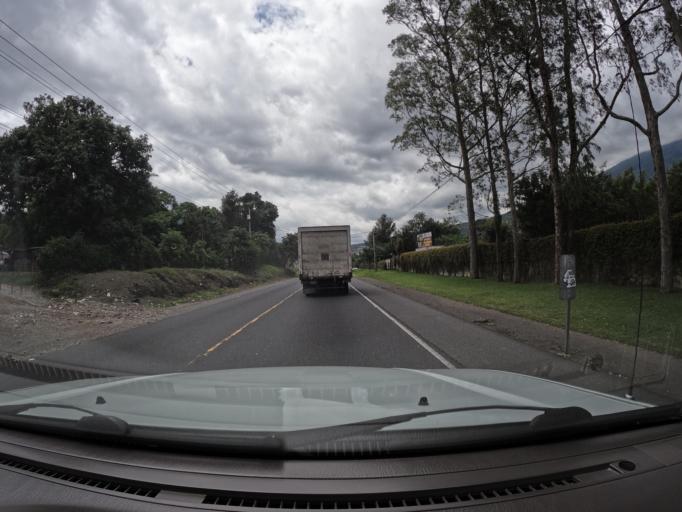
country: GT
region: Sacatepequez
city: Alotenango
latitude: 14.4753
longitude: -90.8100
